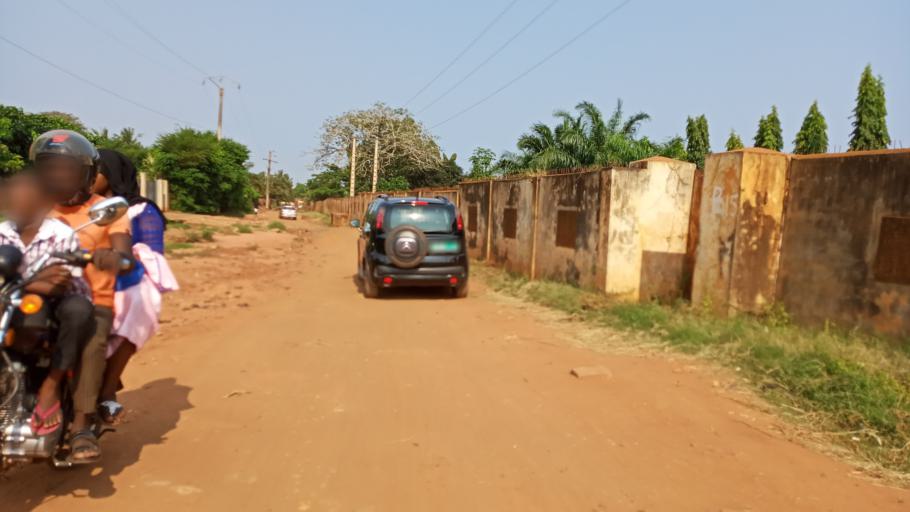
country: TG
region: Maritime
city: Lome
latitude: 6.2084
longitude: 1.2016
